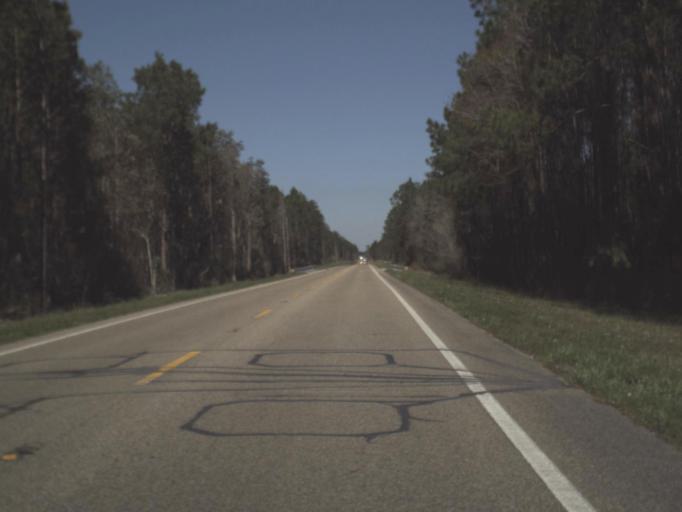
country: US
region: Florida
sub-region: Gulf County
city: Port Saint Joe
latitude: 29.8616
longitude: -85.2437
